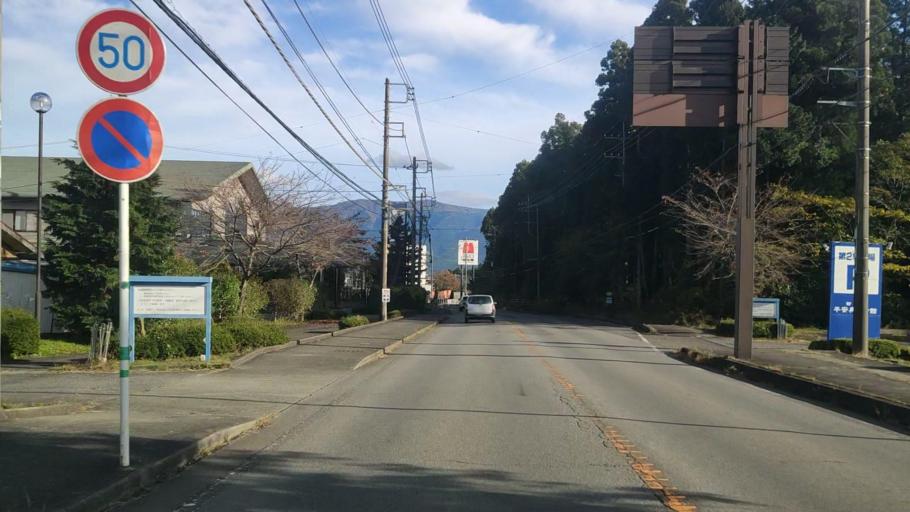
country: JP
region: Shizuoka
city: Gotemba
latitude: 35.3100
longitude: 138.9072
